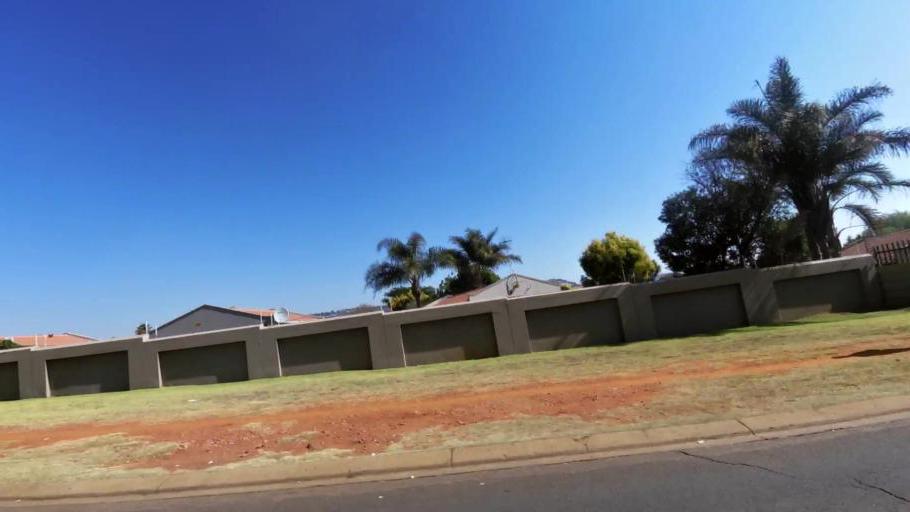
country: ZA
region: Gauteng
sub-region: City of Johannesburg Metropolitan Municipality
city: Roodepoort
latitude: -26.1423
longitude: 27.9359
